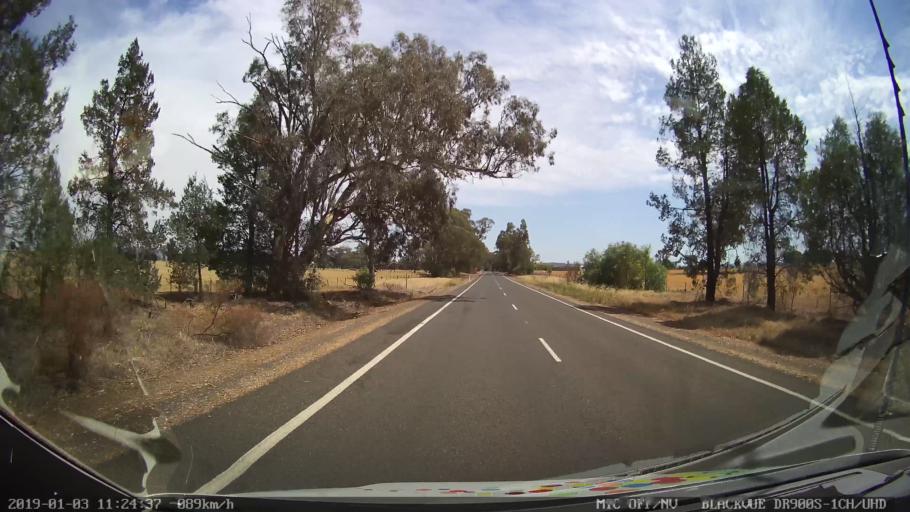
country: AU
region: New South Wales
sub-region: Weddin
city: Grenfell
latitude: -34.0492
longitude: 148.2338
